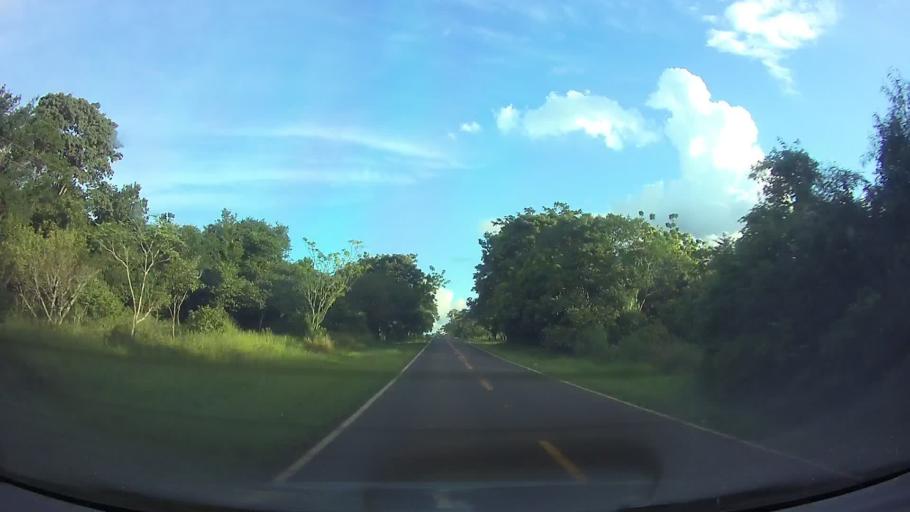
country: PY
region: Paraguari
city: Ybycui
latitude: -25.9574
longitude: -57.0903
